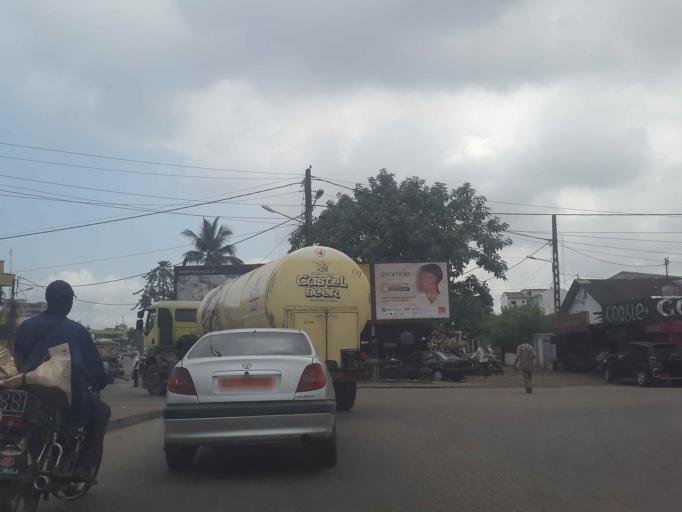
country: CM
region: Littoral
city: Douala
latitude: 4.0323
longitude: 9.6951
